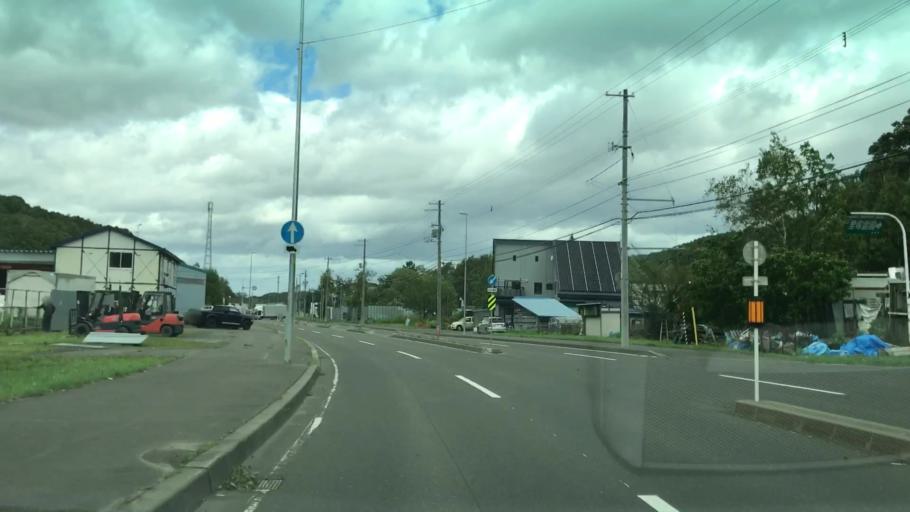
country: JP
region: Hokkaido
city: Kitahiroshima
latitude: 42.9680
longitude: 141.4549
